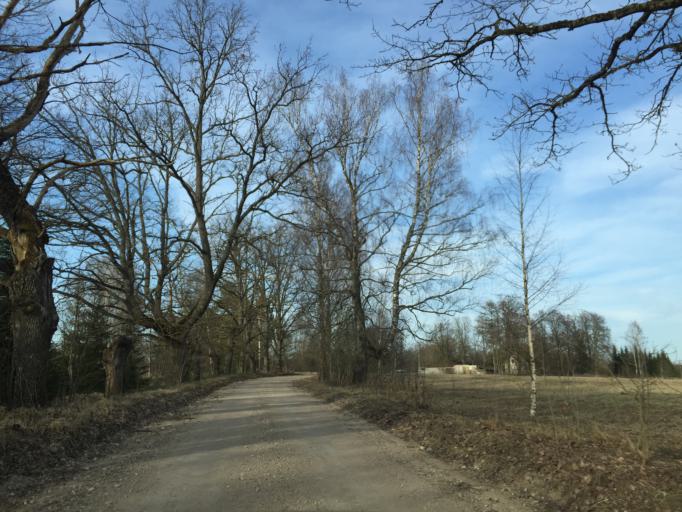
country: LV
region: Kegums
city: Kegums
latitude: 56.8063
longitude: 24.7787
